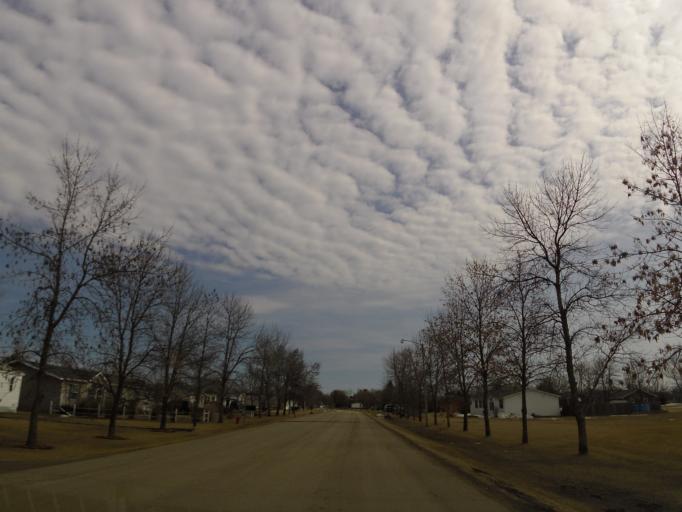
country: US
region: North Dakota
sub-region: Walsh County
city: Grafton
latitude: 48.2934
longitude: -97.3815
